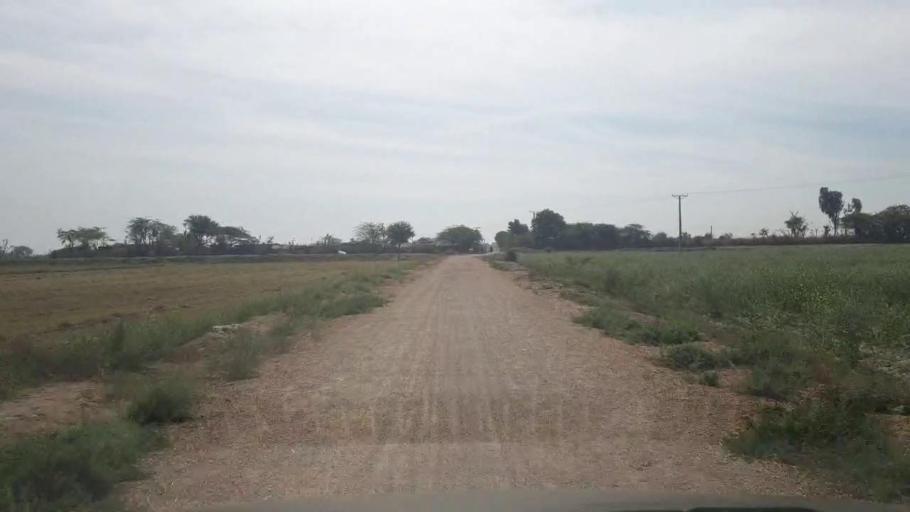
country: PK
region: Sindh
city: Umarkot
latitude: 25.3549
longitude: 69.6066
